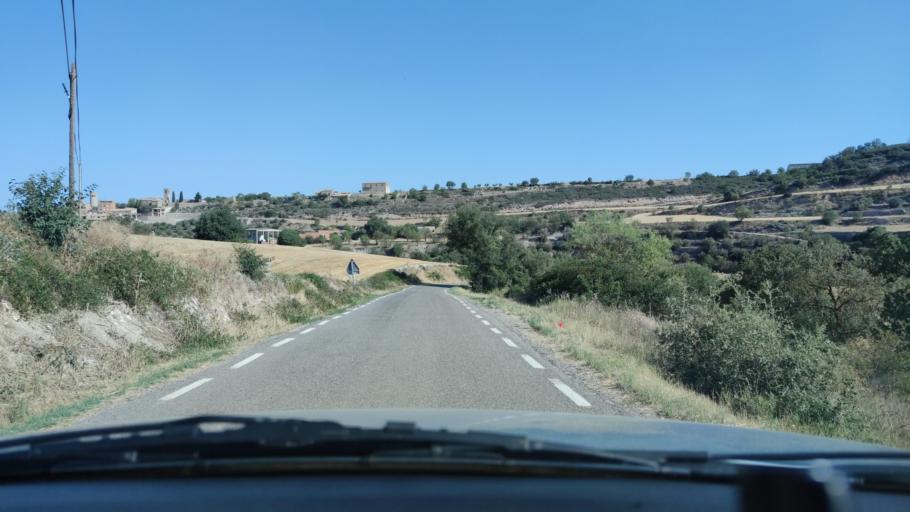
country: ES
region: Catalonia
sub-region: Provincia de Lleida
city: Ivorra
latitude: 41.7351
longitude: 1.3557
